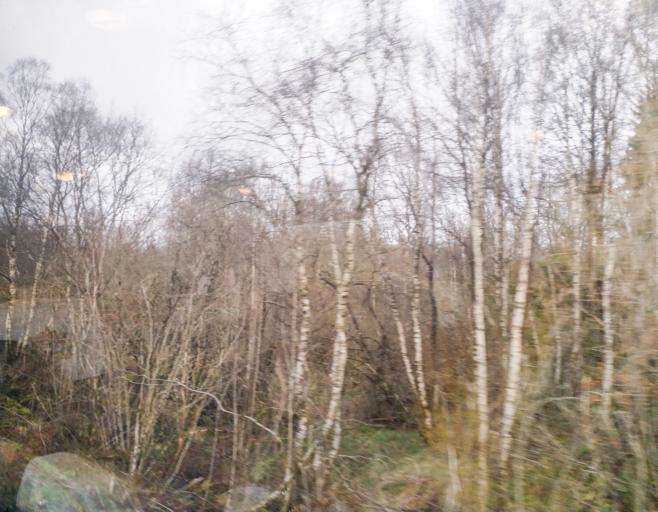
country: GB
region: Scotland
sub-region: Highland
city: Spean Bridge
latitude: 56.8886
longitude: -4.8630
